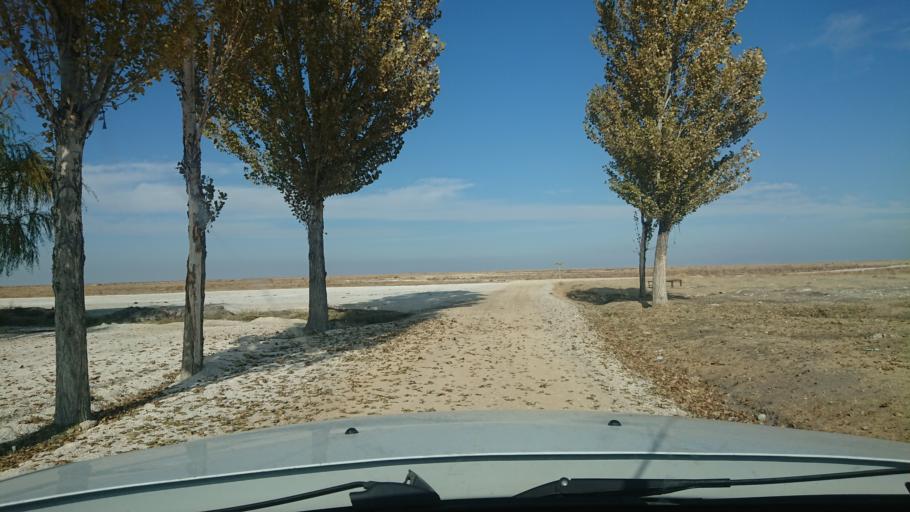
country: TR
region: Aksaray
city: Eskil
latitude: 38.4748
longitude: 33.4576
